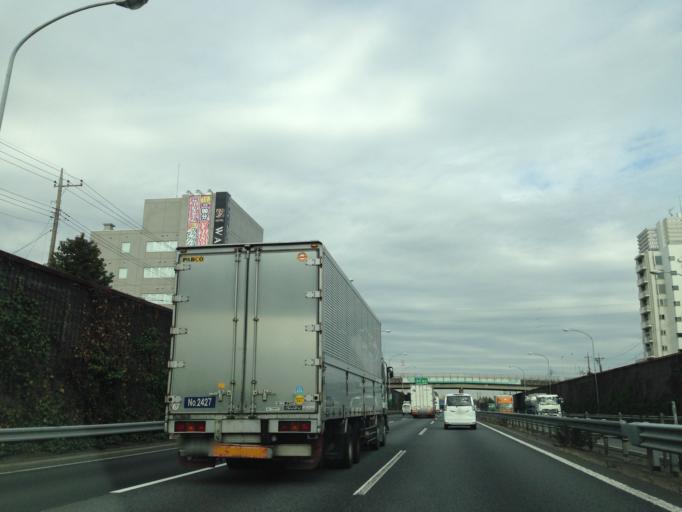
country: JP
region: Saitama
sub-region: Kawaguchi-shi
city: Hatogaya-honcho
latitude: 35.8686
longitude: 139.7347
